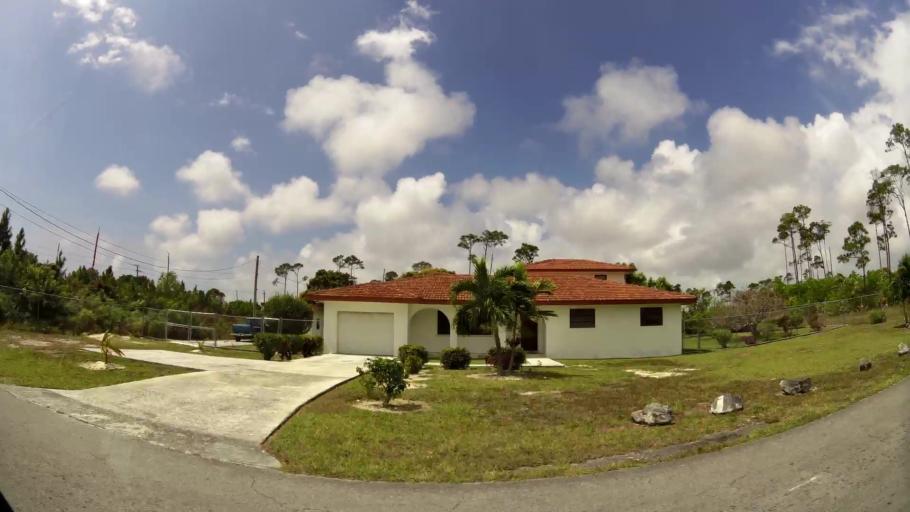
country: BS
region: Freeport
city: Lucaya
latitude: 26.5228
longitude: -78.6572
